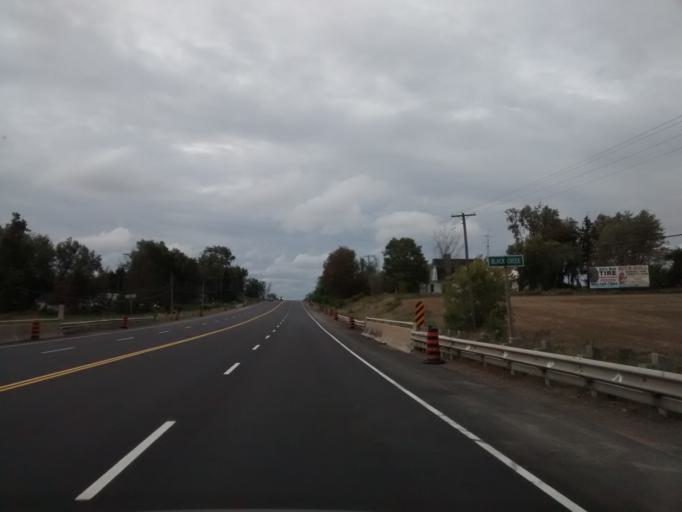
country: CA
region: Ontario
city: Ancaster
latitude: 43.0996
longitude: -79.9402
